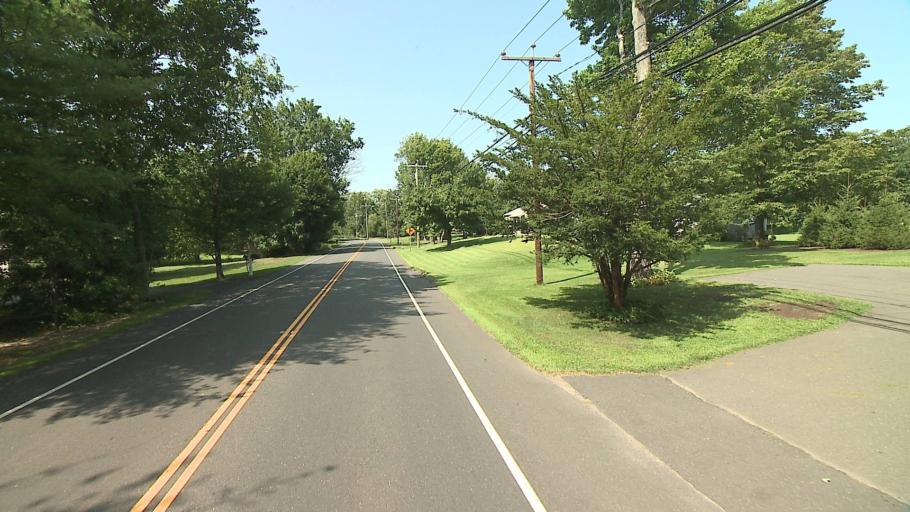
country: US
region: Connecticut
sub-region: Fairfield County
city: Newtown
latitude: 41.4478
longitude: -73.3762
